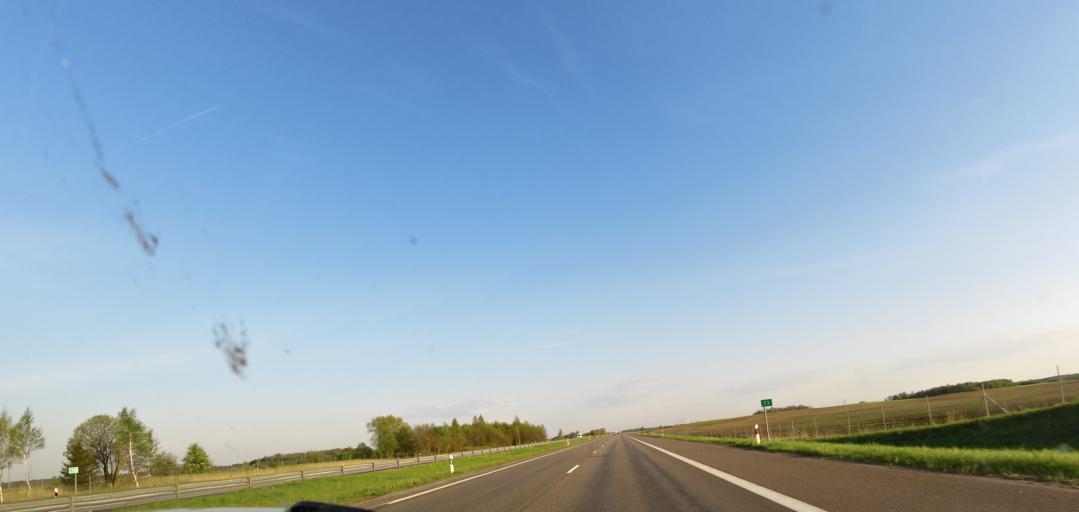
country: LT
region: Vilnius County
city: Ukmerge
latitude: 55.1670
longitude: 24.8162
